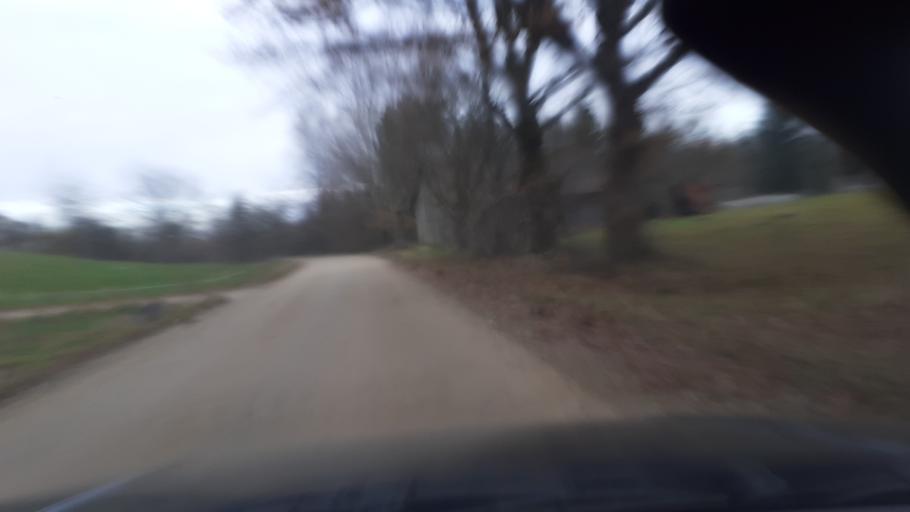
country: LV
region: Alsunga
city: Alsunga
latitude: 56.9722
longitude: 21.6661
